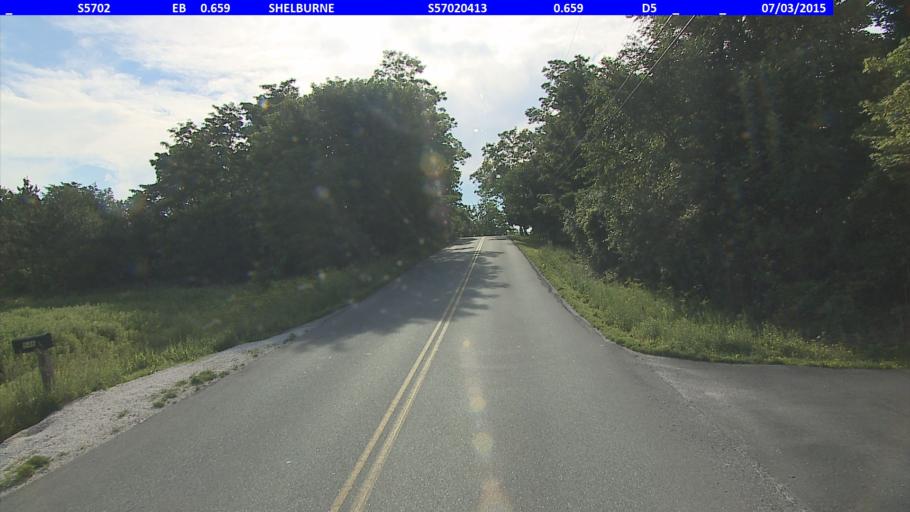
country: US
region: Vermont
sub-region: Chittenden County
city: South Burlington
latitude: 44.4083
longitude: -73.1849
